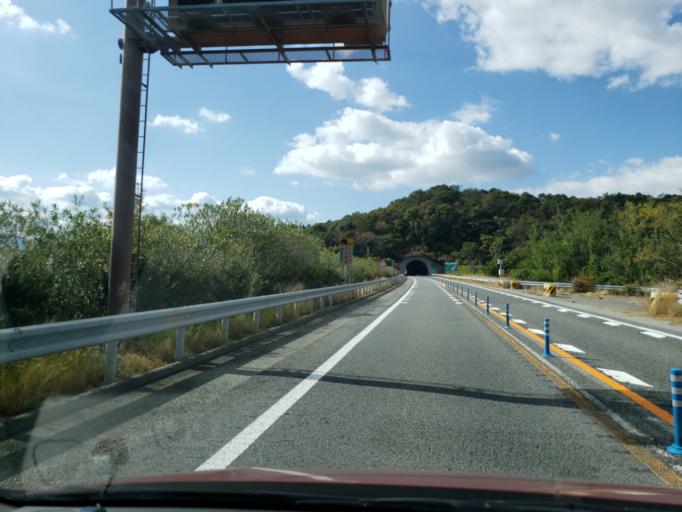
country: JP
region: Tokushima
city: Kamojimacho-jogejima
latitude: 34.1162
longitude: 134.3256
